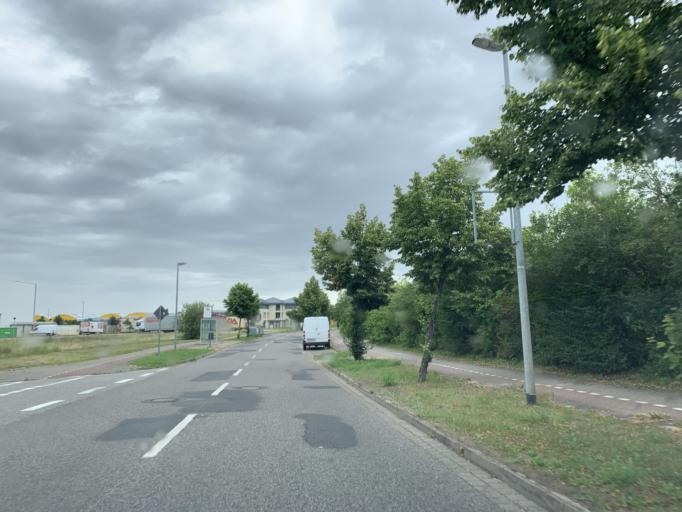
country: DE
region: Mecklenburg-Vorpommern
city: Neubrandenburg
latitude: 53.5186
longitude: 13.2637
